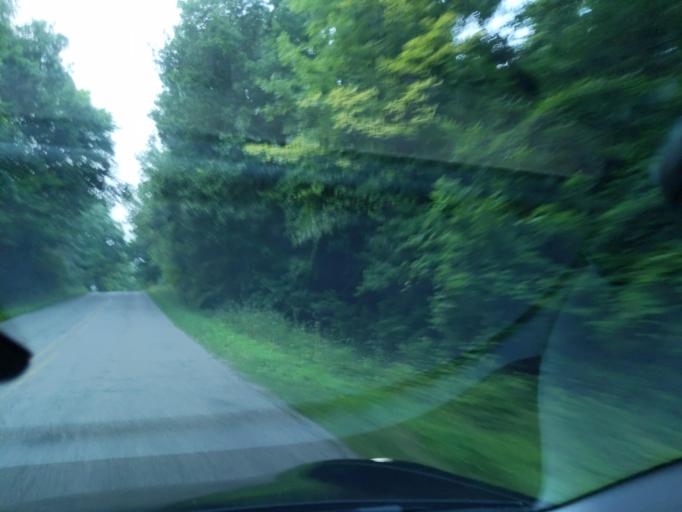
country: US
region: Michigan
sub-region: Ingham County
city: Leslie
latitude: 42.3501
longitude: -84.4924
